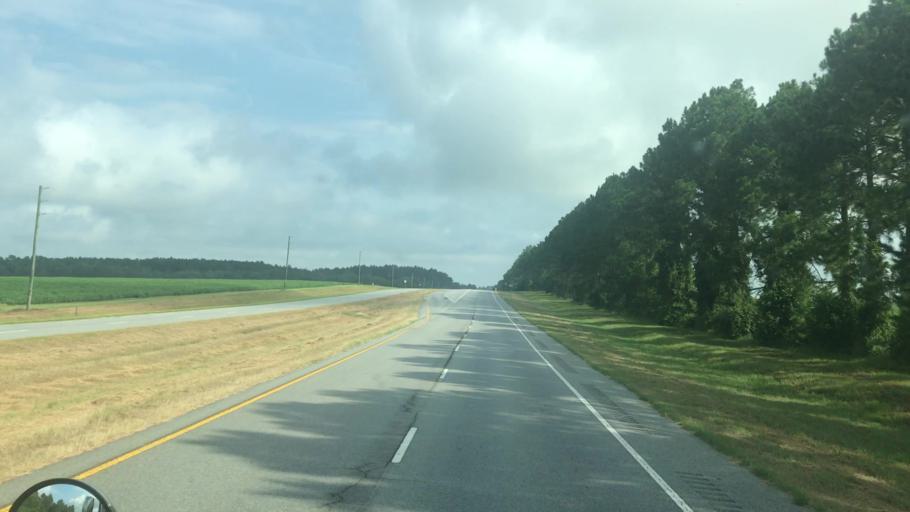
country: US
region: Georgia
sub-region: Miller County
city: Colquitt
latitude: 31.1897
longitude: -84.7644
